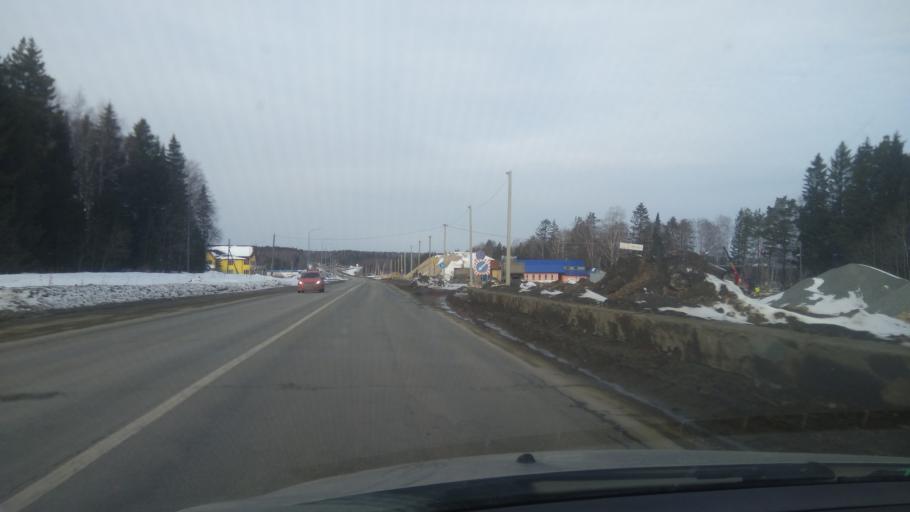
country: RU
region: Sverdlovsk
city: Bisert'
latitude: 56.8295
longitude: 59.0498
